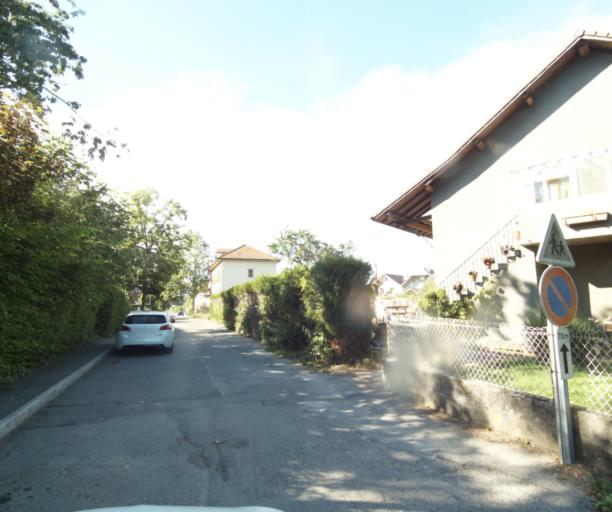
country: FR
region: Rhone-Alpes
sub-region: Departement de la Haute-Savoie
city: Sciez
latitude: 46.3541
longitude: 6.3529
